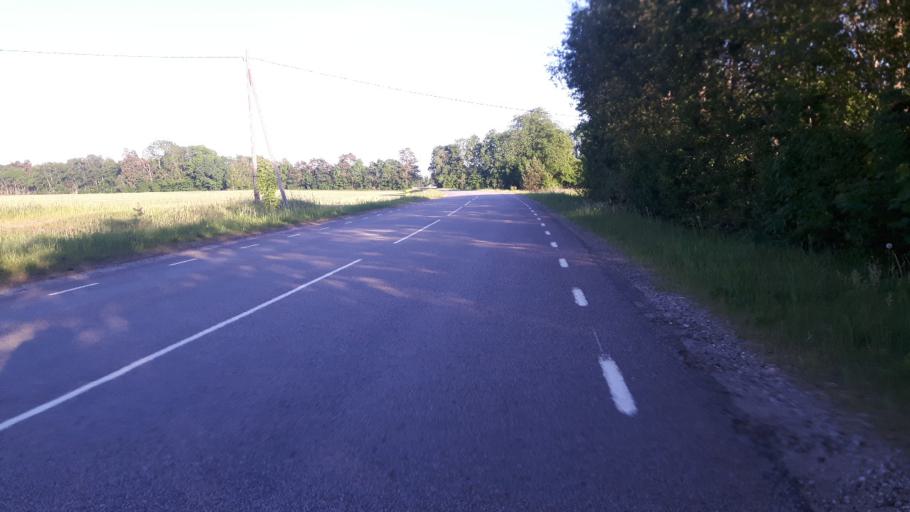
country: EE
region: Raplamaa
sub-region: Jaervakandi vald
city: Jarvakandi
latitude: 58.8028
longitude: 24.9212
